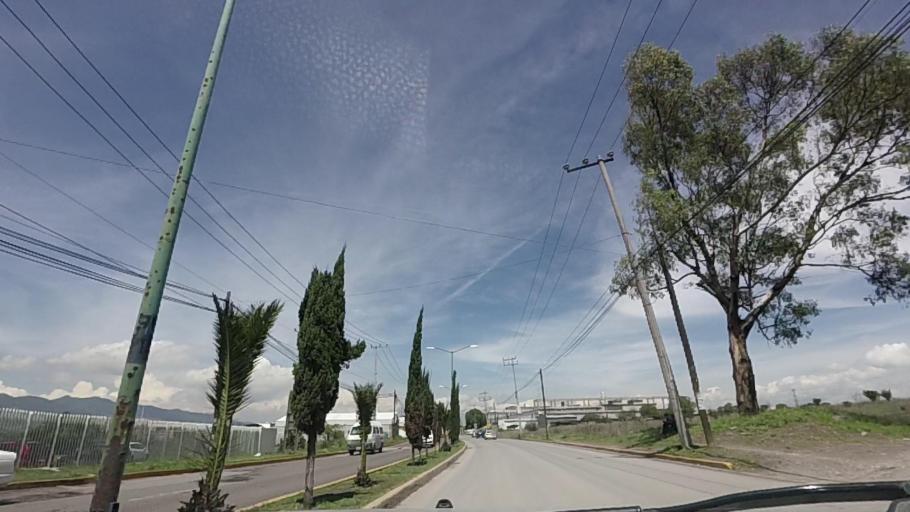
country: MX
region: Mexico
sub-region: Huehuetoca
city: Colonia Santa Teresa
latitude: 19.8294
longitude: -99.2312
